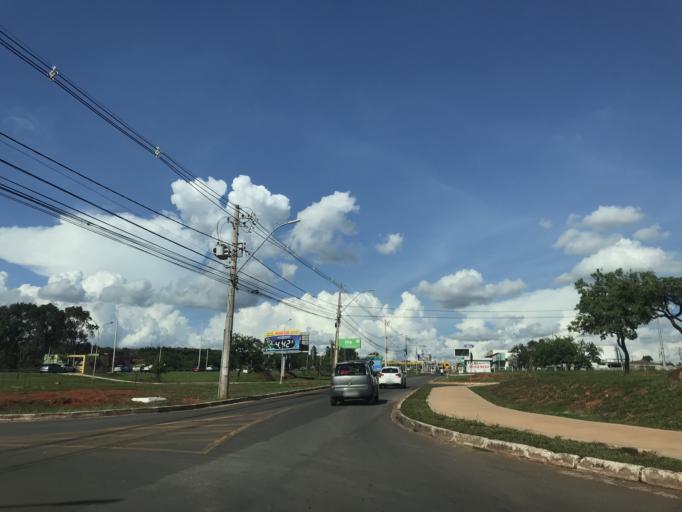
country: BR
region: Federal District
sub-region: Brasilia
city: Brasilia
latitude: -15.6970
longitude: -47.8754
